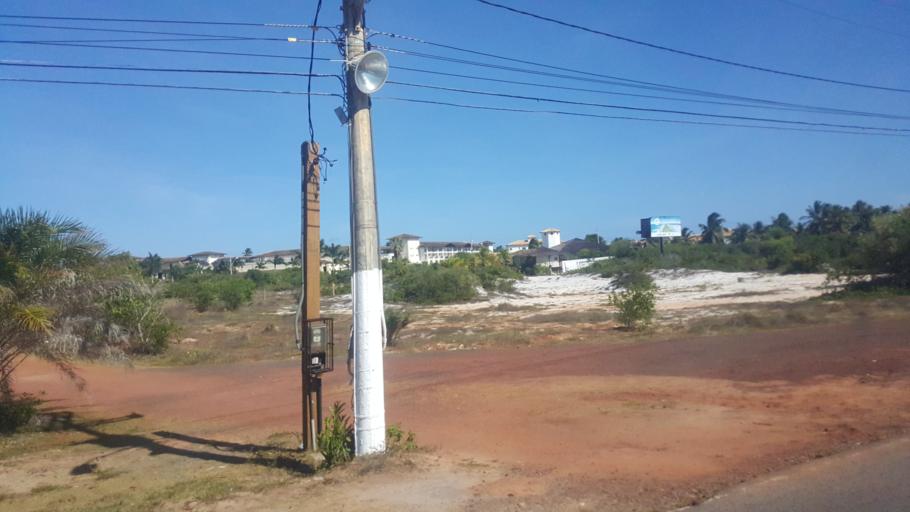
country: BR
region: Bahia
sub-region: Mata De Sao Joao
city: Mata de Sao Joao
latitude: -12.4380
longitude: -37.9228
